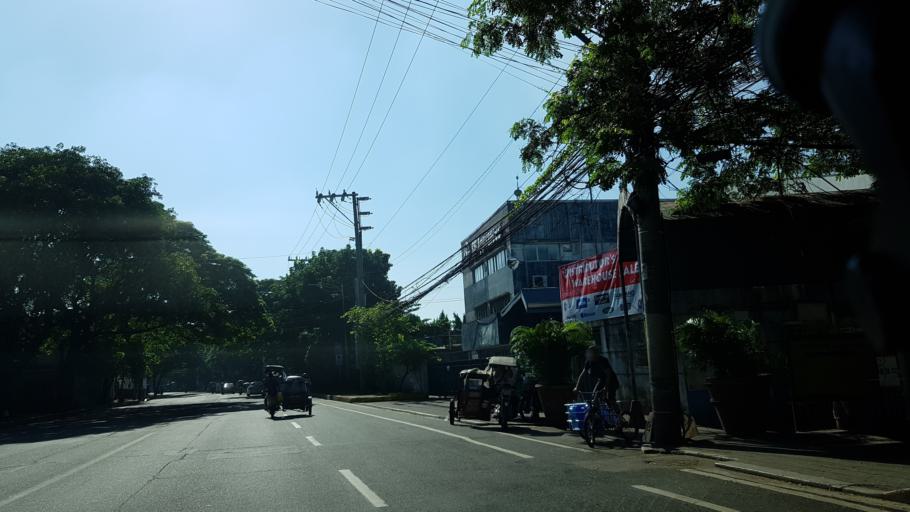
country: PH
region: Metro Manila
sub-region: Pasig
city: Pasig City
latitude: 14.5680
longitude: 121.0875
